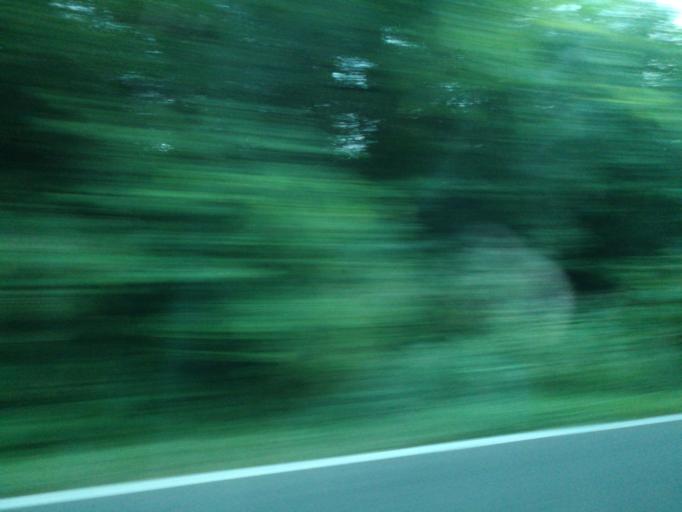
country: RO
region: Constanta
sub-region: Comuna Douazeci si Trei August
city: Douazeci si Trei August
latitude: 43.8588
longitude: 28.5839
